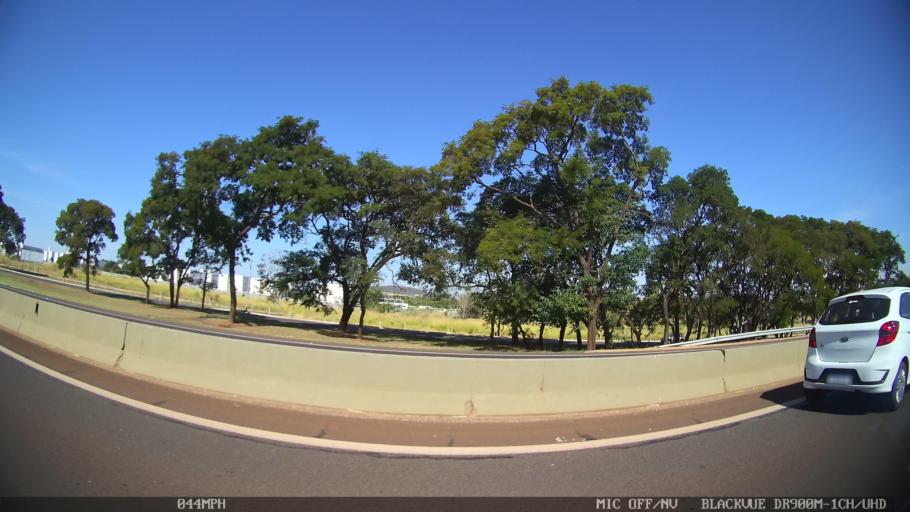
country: BR
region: Sao Paulo
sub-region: Ribeirao Preto
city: Ribeirao Preto
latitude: -21.2095
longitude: -47.7675
